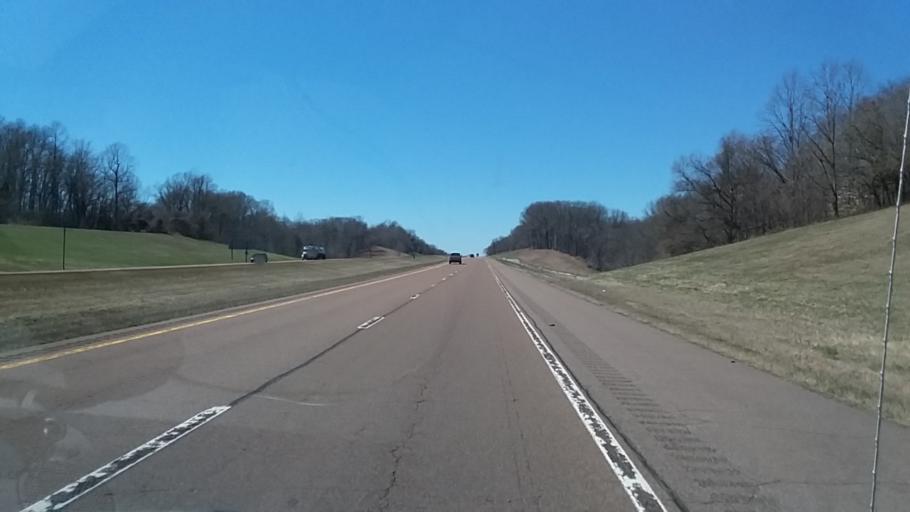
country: US
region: Tennessee
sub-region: Dyer County
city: Dyersburg
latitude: 36.0731
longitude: -89.4745
